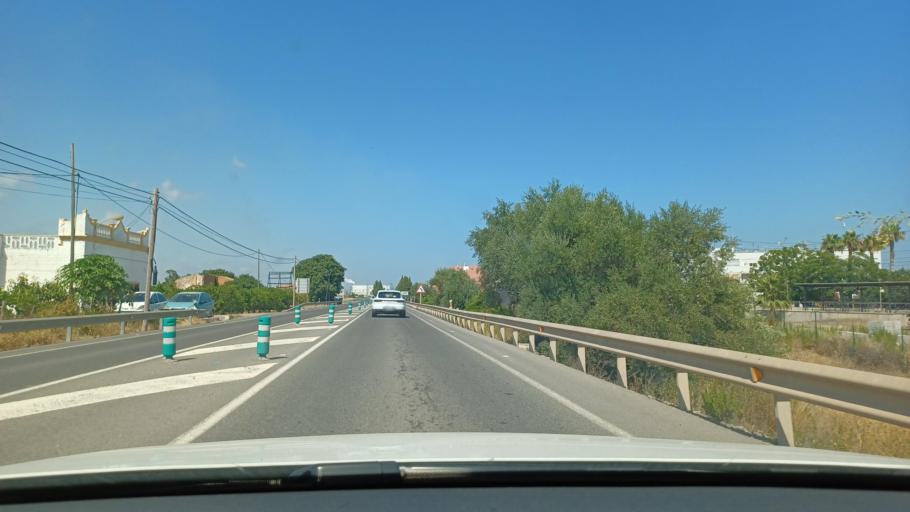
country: ES
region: Valencia
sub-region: Provincia de Castello
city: Chilches
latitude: 39.7827
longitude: -0.1913
